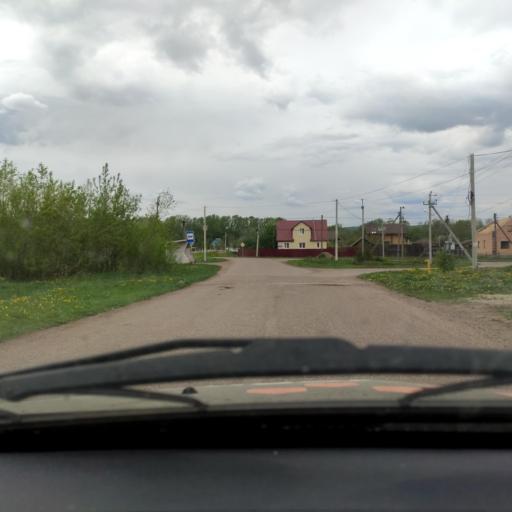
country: RU
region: Bashkortostan
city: Avdon
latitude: 54.5969
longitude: 55.7071
